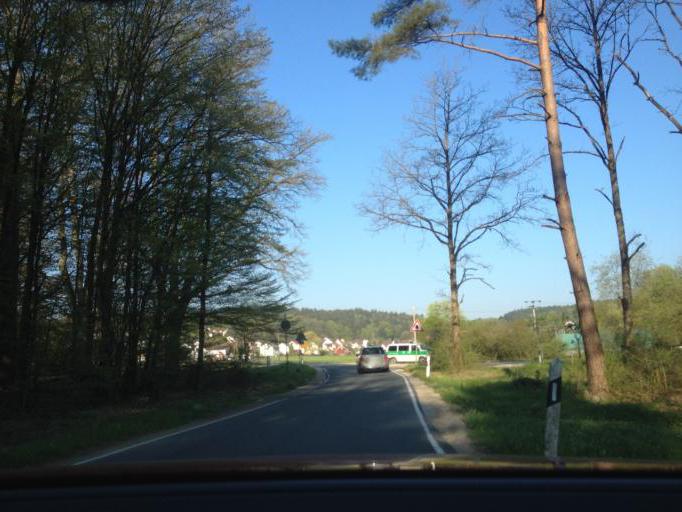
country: DE
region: Bavaria
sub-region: Regierungsbezirk Mittelfranken
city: Leinburg
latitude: 49.4358
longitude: 11.2642
